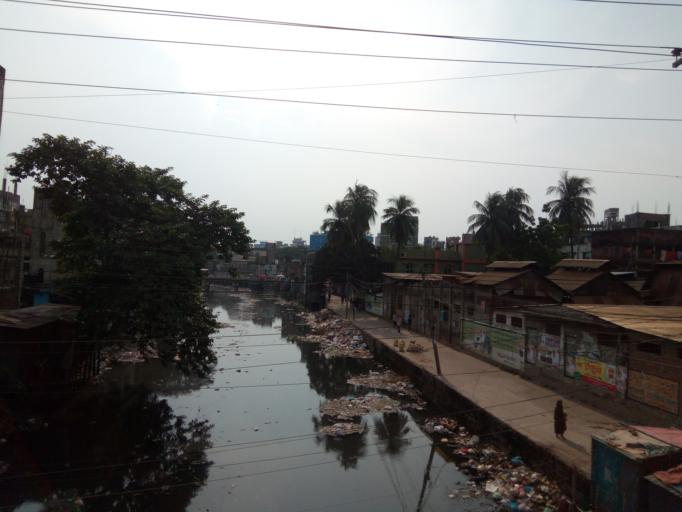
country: BD
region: Dhaka
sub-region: Dhaka
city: Dhaka
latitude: 23.6978
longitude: 90.3980
